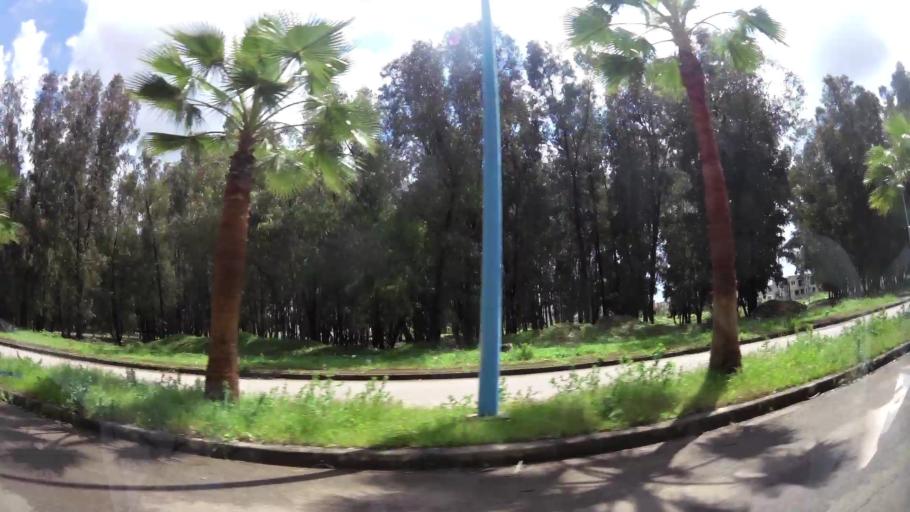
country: MA
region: Chaouia-Ouardigha
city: Nouaseur
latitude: 33.3994
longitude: -7.5603
